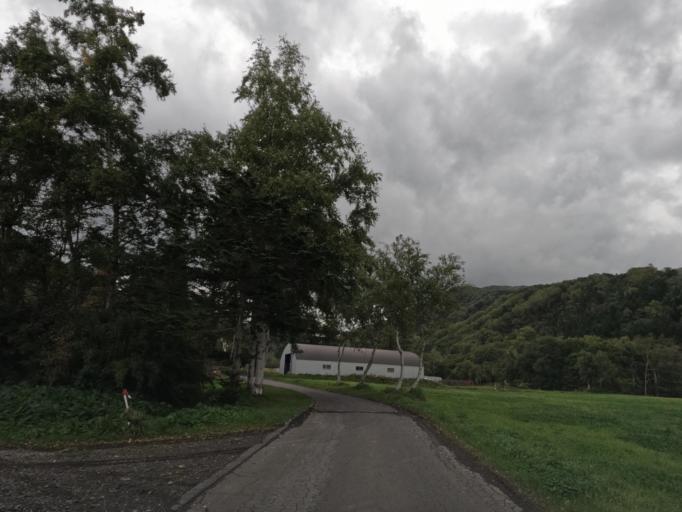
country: JP
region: Hokkaido
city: Date
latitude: 42.5007
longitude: 140.9063
